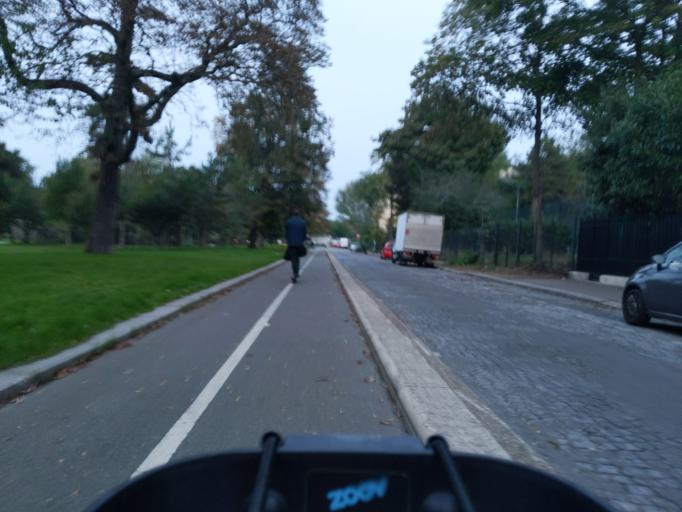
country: FR
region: Ile-de-France
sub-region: Departement des Hauts-de-Seine
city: Neuilly-sur-Seine
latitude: 48.8683
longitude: 2.2711
